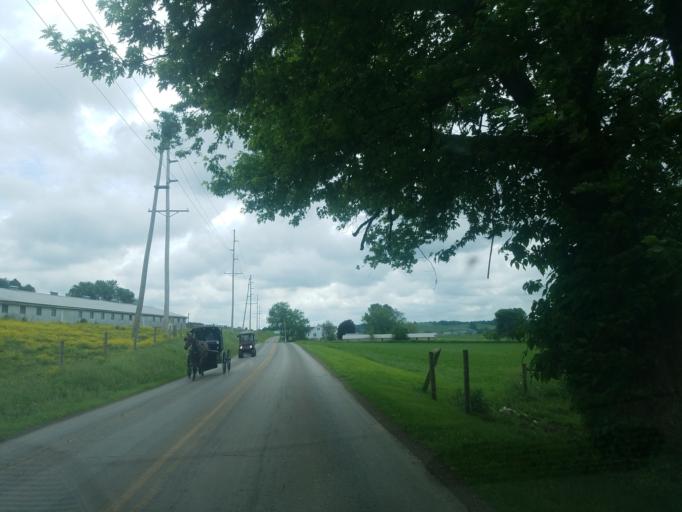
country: US
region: Ohio
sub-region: Tuscarawas County
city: Sugarcreek
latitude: 40.5314
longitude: -81.7377
